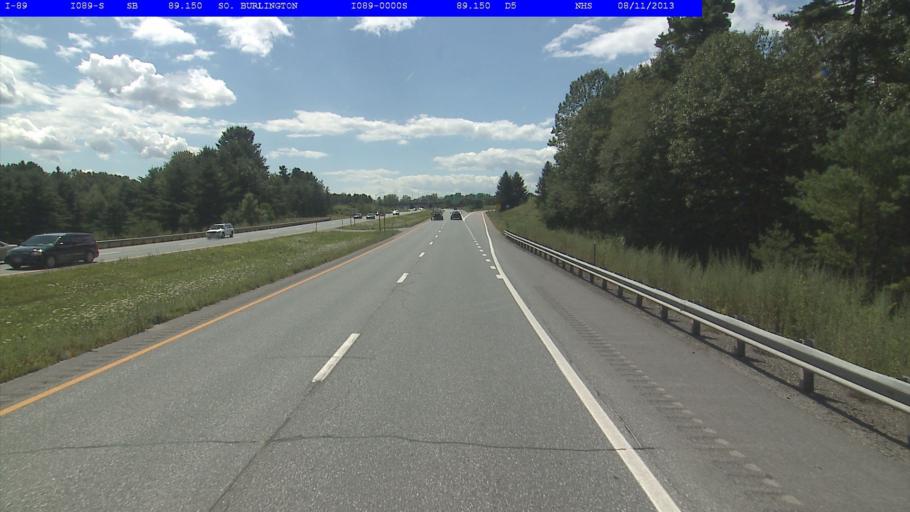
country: US
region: Vermont
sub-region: Chittenden County
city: South Burlington
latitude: 44.4752
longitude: -73.1803
